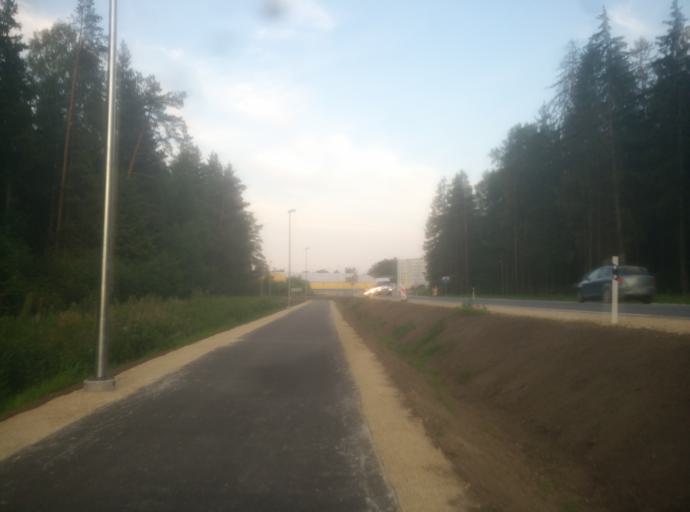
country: LV
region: Ogre
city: Ogre
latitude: 56.8279
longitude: 24.5957
